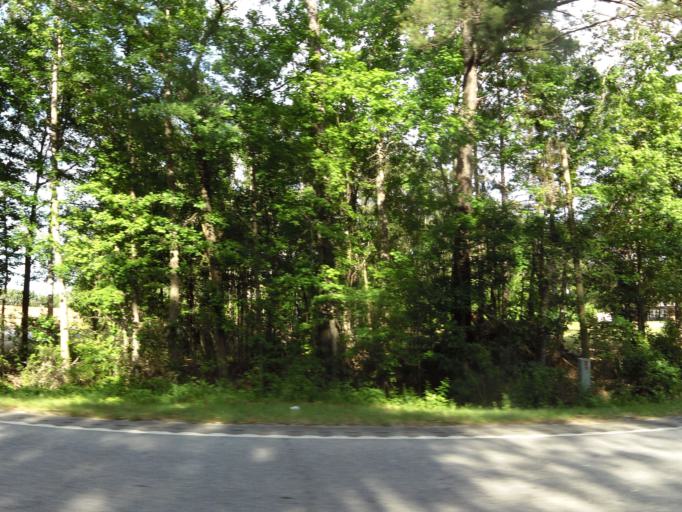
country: US
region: South Carolina
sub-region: Hampton County
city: Estill
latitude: 32.8468
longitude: -81.2390
